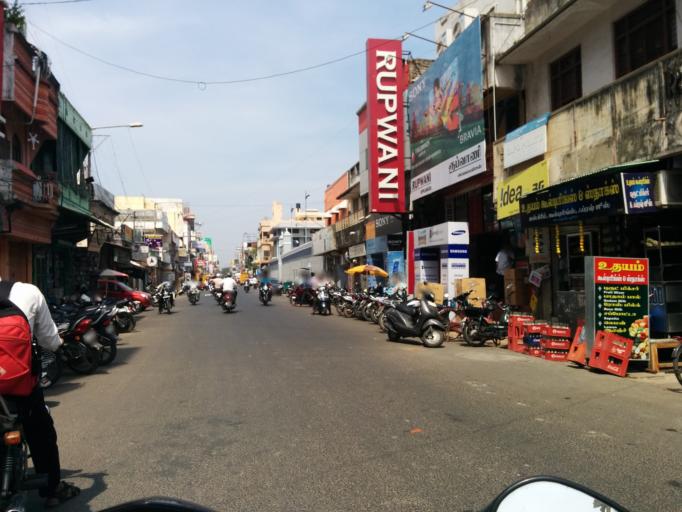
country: IN
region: Pondicherry
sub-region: Puducherry
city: Puducherry
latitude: 11.9325
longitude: 79.8286
